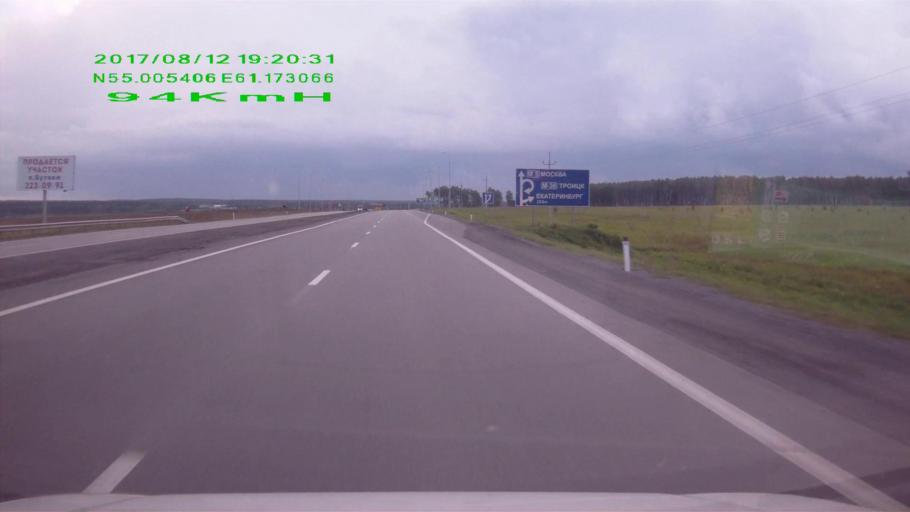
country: RU
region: Chelyabinsk
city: Poletayevo
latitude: 55.0053
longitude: 61.1692
